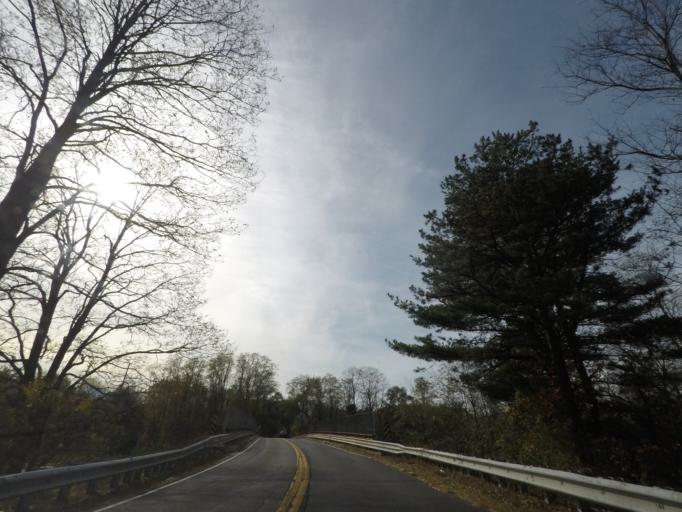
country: US
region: New York
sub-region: Albany County
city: Westmere
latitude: 42.7256
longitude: -73.8880
